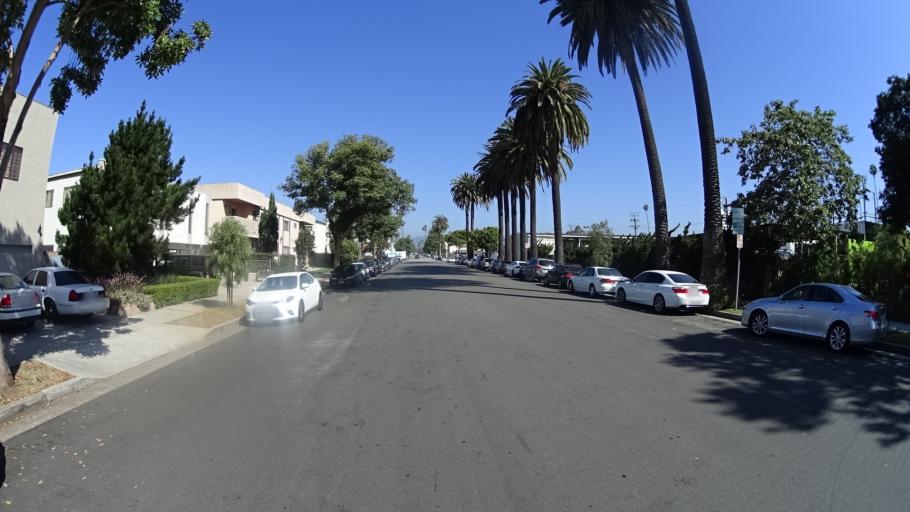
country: US
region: California
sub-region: Los Angeles County
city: Santa Monica
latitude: 34.0217
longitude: -118.4867
